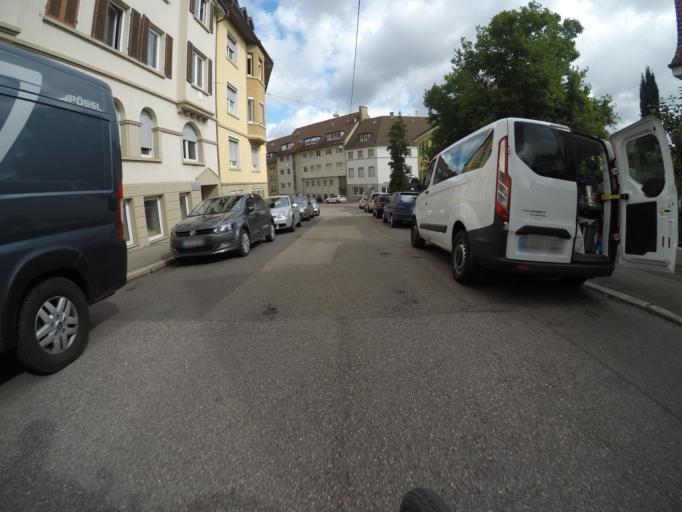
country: DE
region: Baden-Wuerttemberg
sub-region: Regierungsbezirk Stuttgart
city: Stuttgart
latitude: 48.7582
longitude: 9.1582
